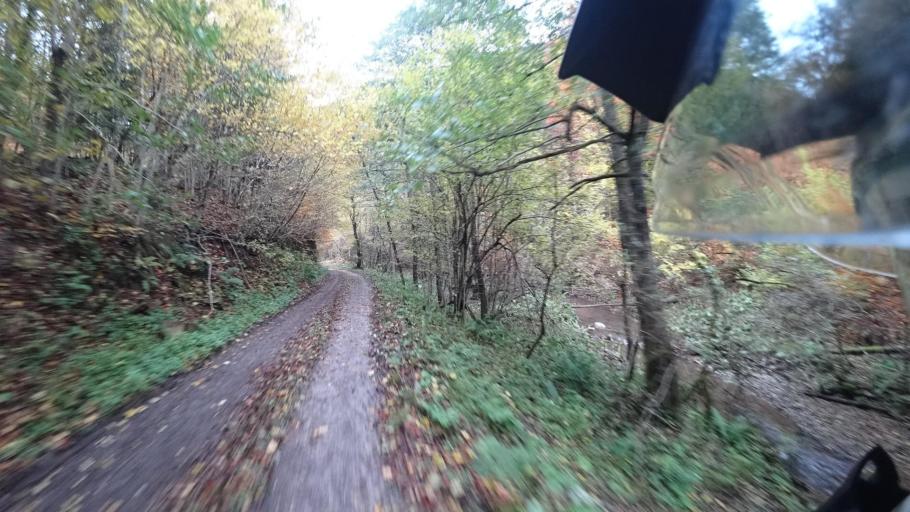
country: SI
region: Kostel
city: Kostel
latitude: 45.4258
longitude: 14.9565
